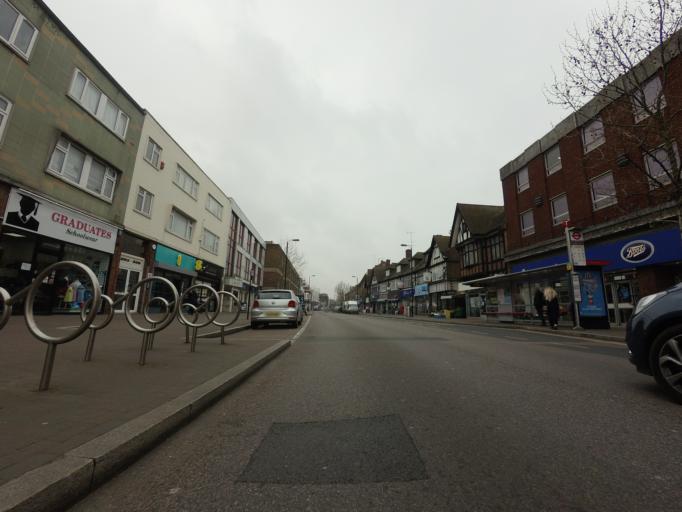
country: GB
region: England
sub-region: Greater London
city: Orpington
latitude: 51.3765
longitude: 0.0998
